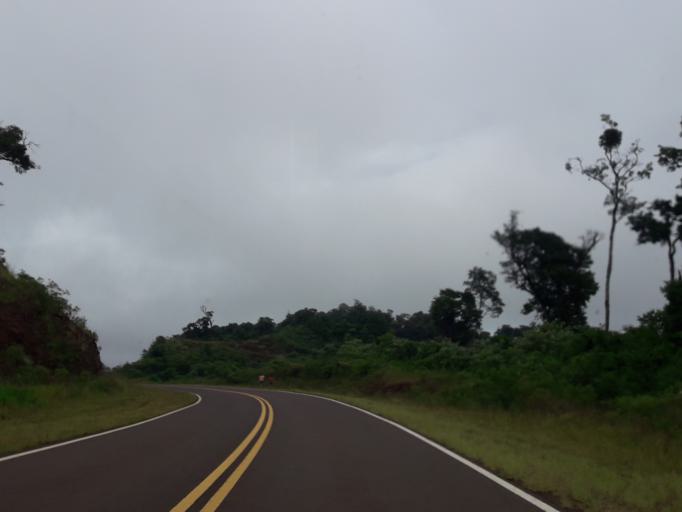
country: AR
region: Misiones
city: Bernardo de Irigoyen
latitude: -26.3997
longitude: -53.8177
